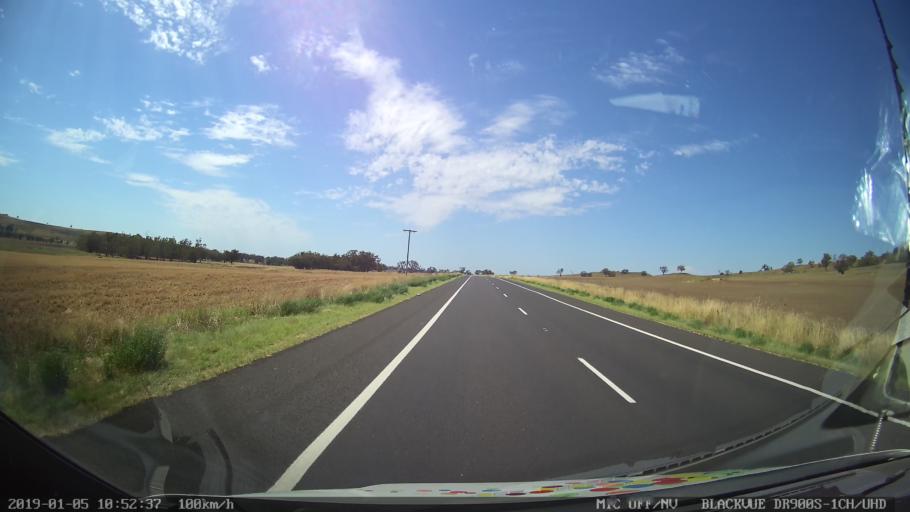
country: AU
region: New South Wales
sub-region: Warrumbungle Shire
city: Coonabarabran
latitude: -31.4339
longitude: 149.1051
